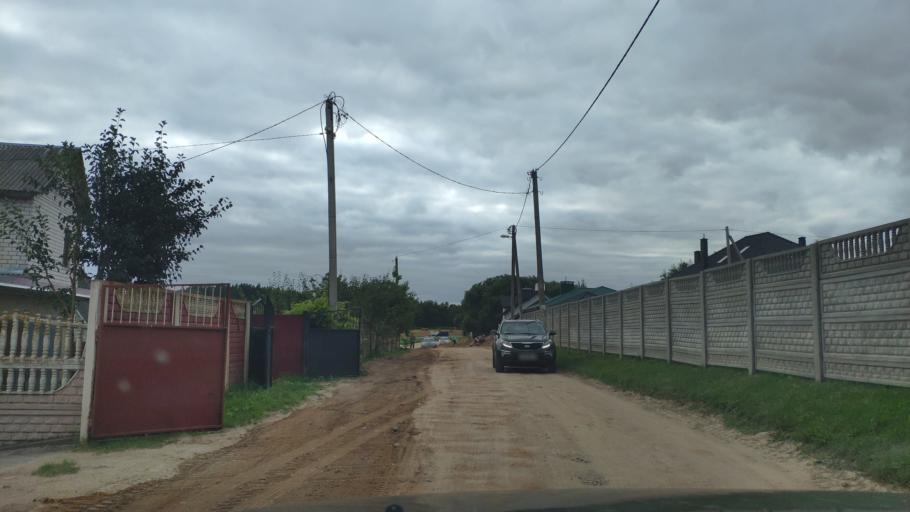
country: BY
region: Minsk
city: Novosel'ye
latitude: 53.9261
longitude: 27.2499
